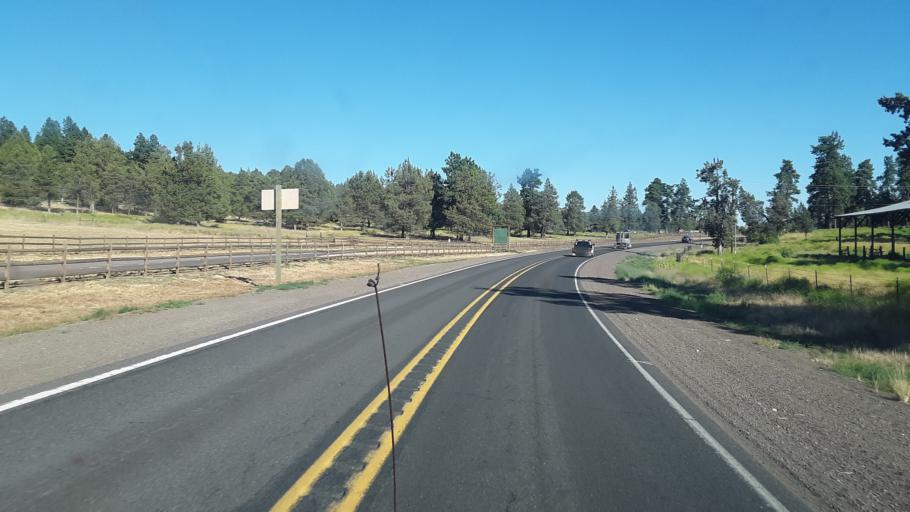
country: US
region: Oregon
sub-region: Klamath County
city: Klamath Falls
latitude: 42.2707
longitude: -121.8815
